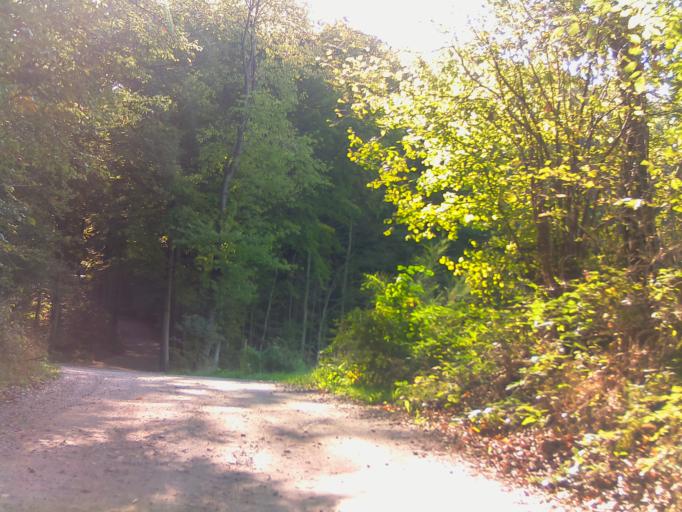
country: DE
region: Hesse
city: Unter-Abtsteinach
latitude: 49.5080
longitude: 8.7580
